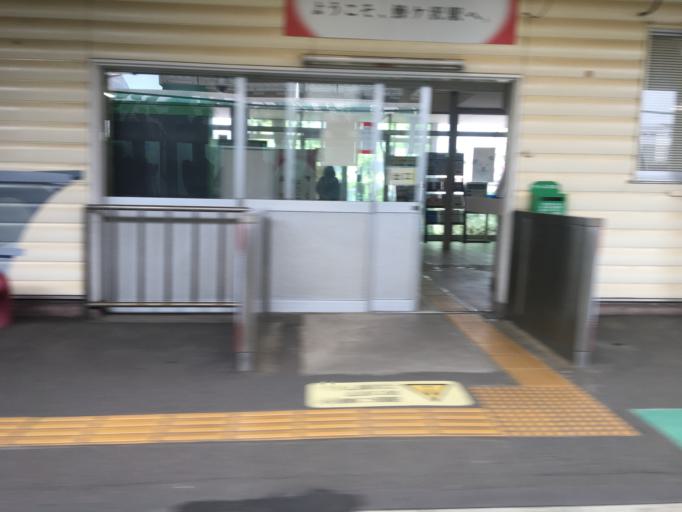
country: JP
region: Aomori
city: Shimokizukuri
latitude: 40.7754
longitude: 140.2206
